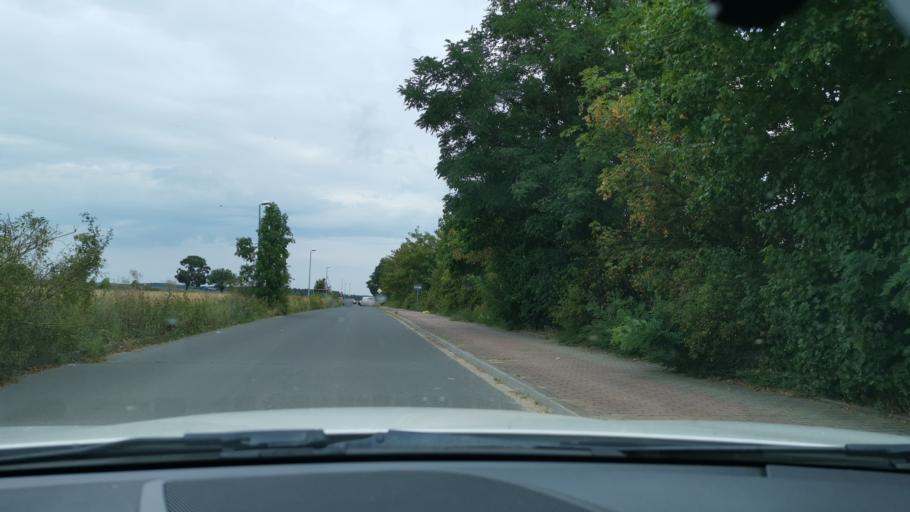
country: DE
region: Brandenburg
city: Luckenwalde
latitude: 52.1017
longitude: 13.1236
